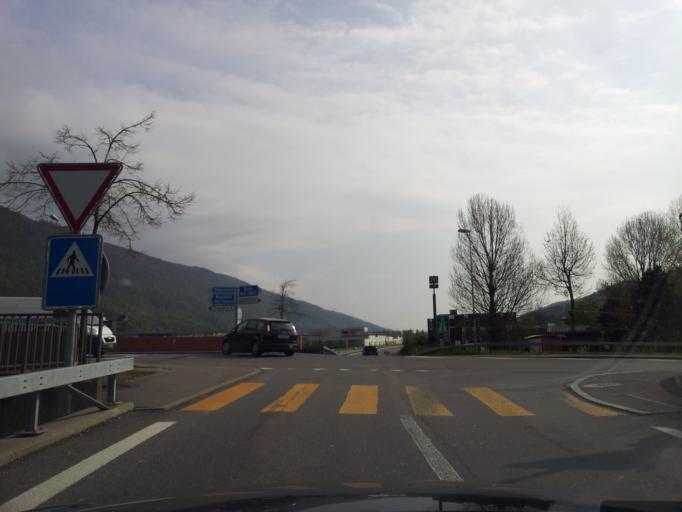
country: CH
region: Bern
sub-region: Biel/Bienne District
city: Orpund
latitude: 47.1587
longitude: 7.2864
